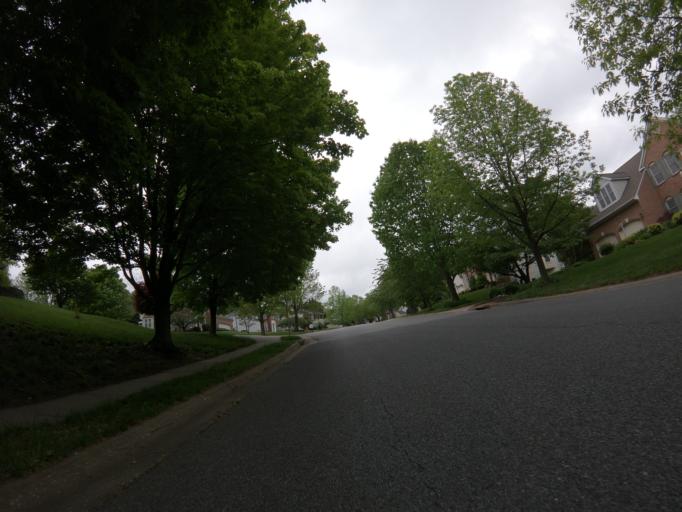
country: US
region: Maryland
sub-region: Howard County
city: Ilchester
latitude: 39.2454
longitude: -76.7882
